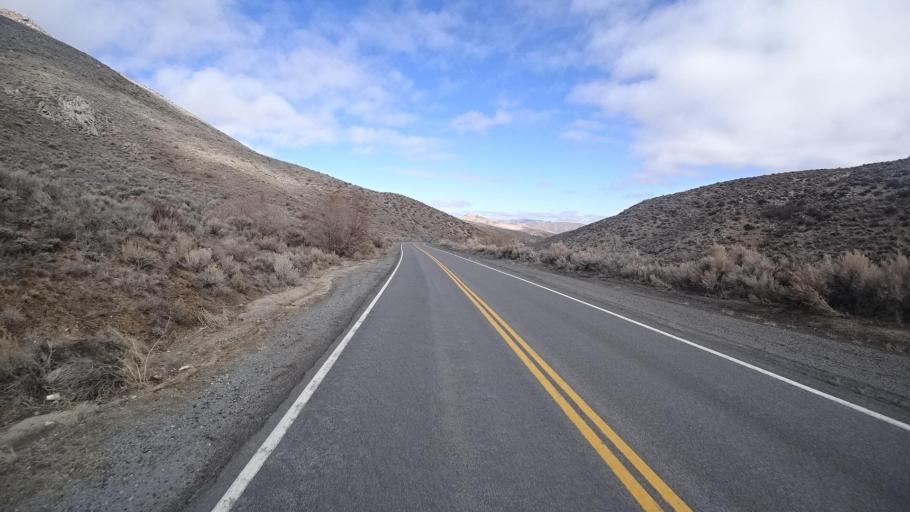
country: US
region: Nevada
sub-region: Washoe County
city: Cold Springs
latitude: 39.8166
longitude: -119.9351
